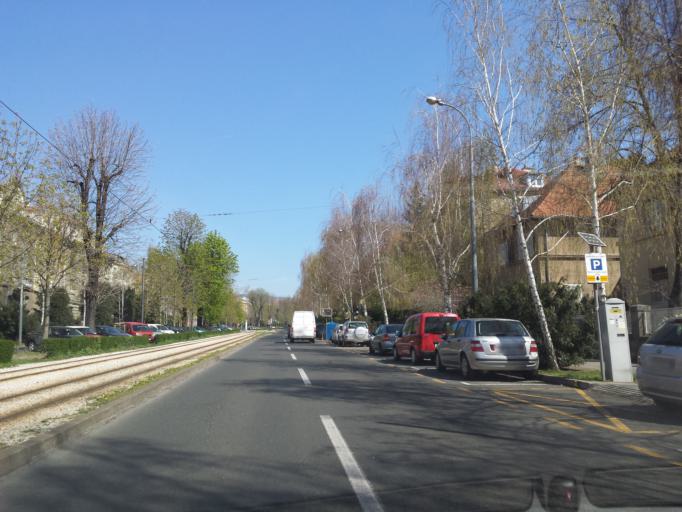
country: HR
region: Grad Zagreb
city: Zagreb
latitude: 45.8209
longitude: 15.9797
